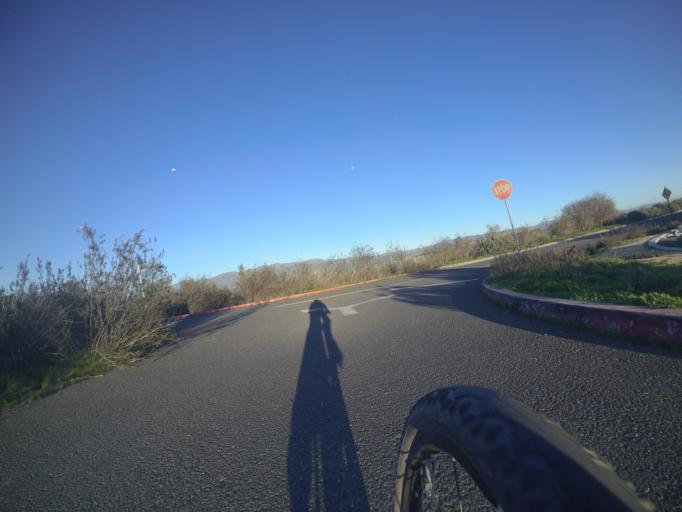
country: US
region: California
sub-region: Santa Clara County
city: Milpitas
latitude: 37.4393
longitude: -121.9589
